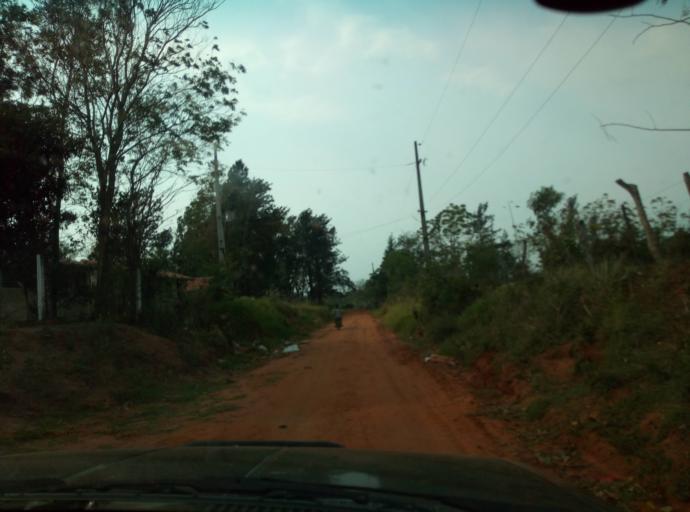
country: PY
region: Caaguazu
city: San Joaquin
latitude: -25.1472
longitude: -56.0974
